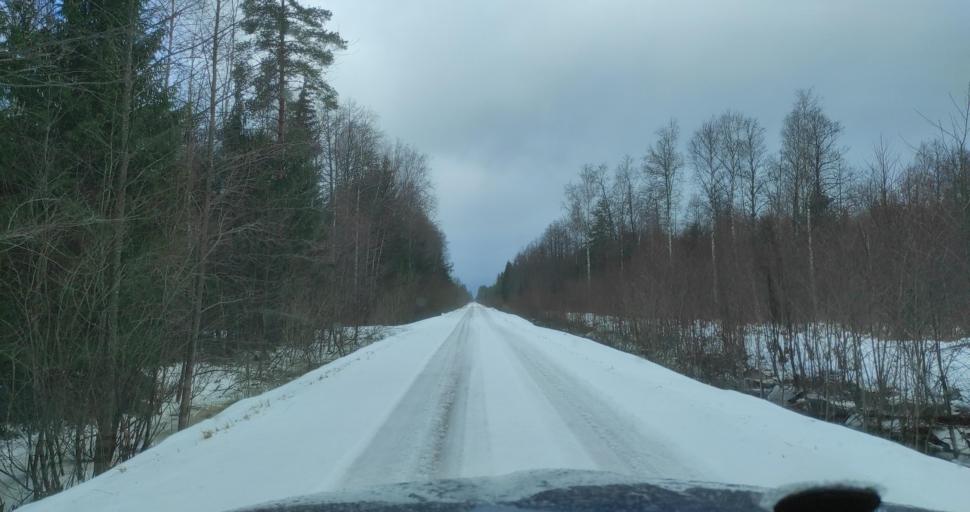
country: LV
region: Dundaga
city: Dundaga
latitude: 57.3969
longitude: 22.1164
